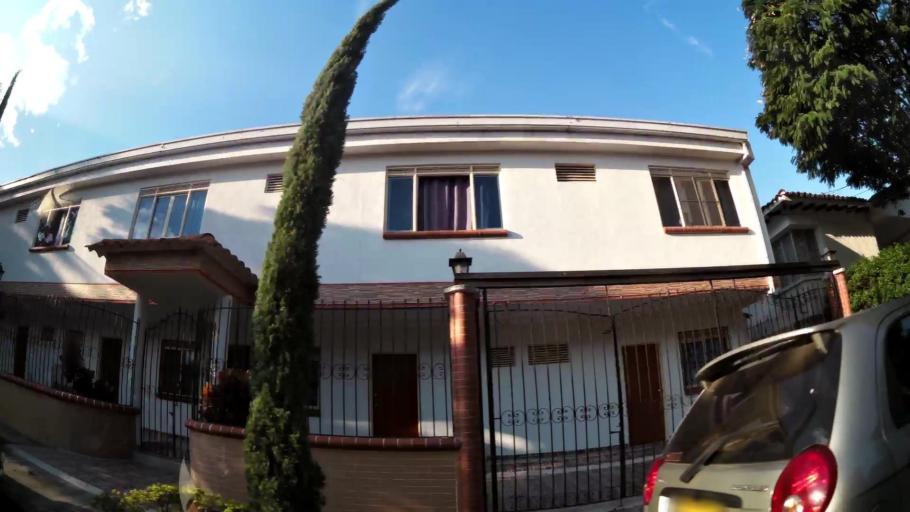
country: CO
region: Valle del Cauca
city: Cali
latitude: 3.4028
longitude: -76.5506
